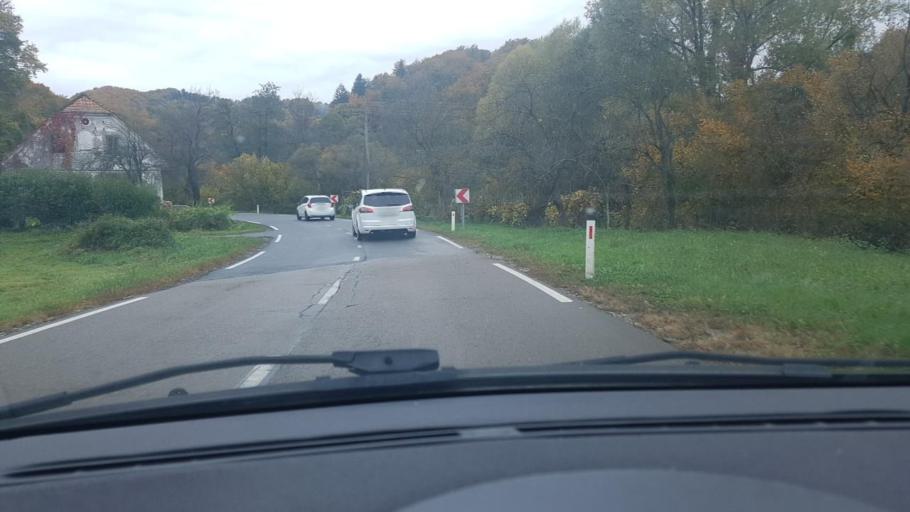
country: SI
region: Majsperk
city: Majsperk
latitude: 46.3259
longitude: 15.7208
